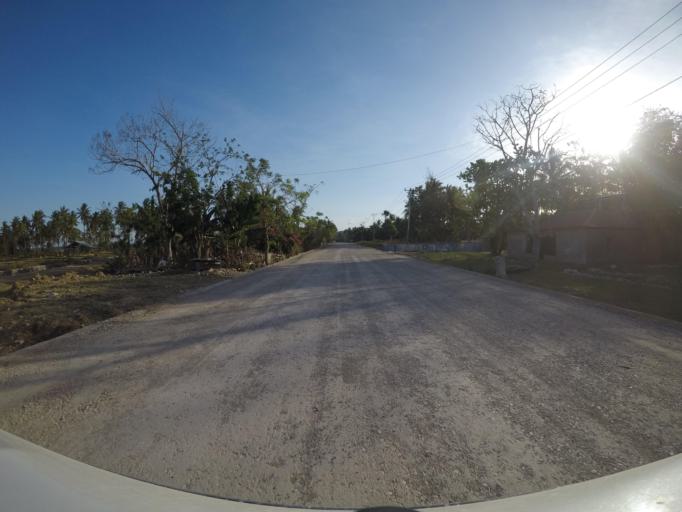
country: TL
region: Viqueque
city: Viqueque
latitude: -8.8088
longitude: 126.5414
